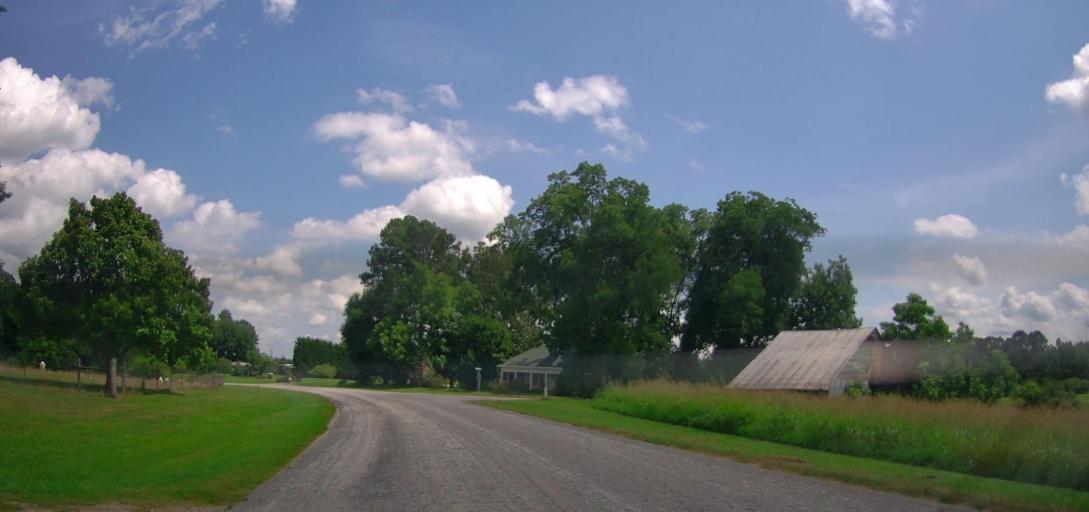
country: US
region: Georgia
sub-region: Carroll County
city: Bowdon
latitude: 33.5149
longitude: -85.3451
